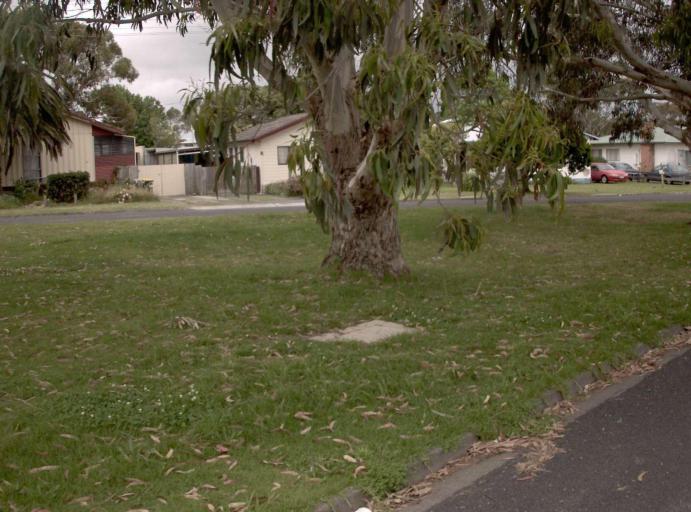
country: AU
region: Victoria
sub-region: Bass Coast
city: North Wonthaggi
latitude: -38.6015
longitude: 145.6007
